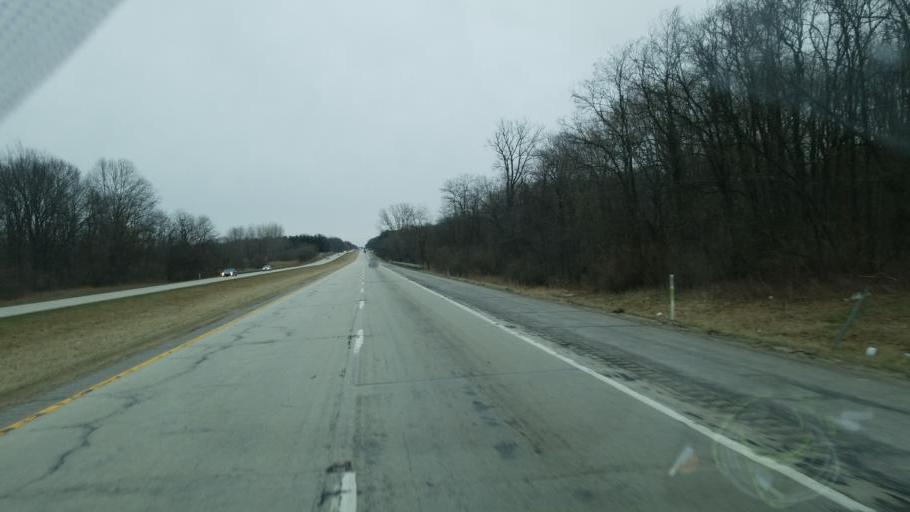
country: US
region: Indiana
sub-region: Starke County
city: Koontz Lake
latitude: 41.3644
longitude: -86.4543
